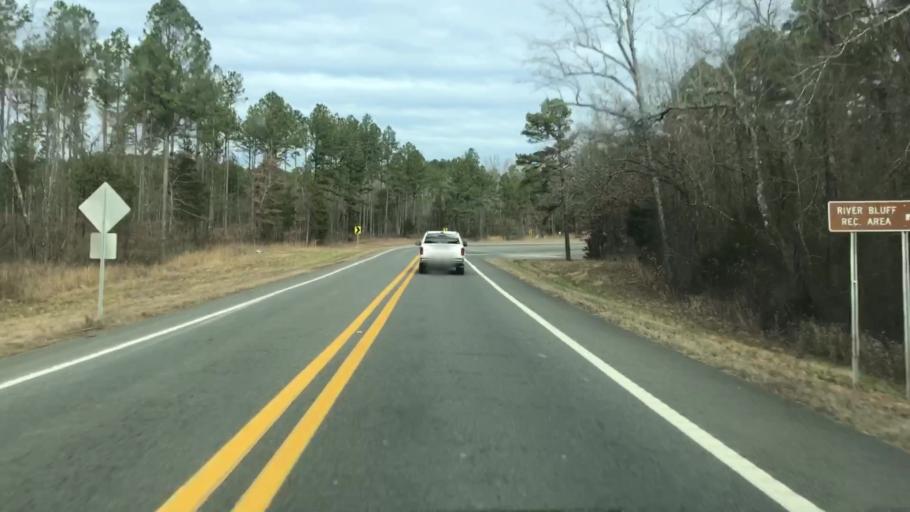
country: US
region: Arkansas
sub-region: Montgomery County
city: Mount Ida
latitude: 34.5921
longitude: -93.6654
